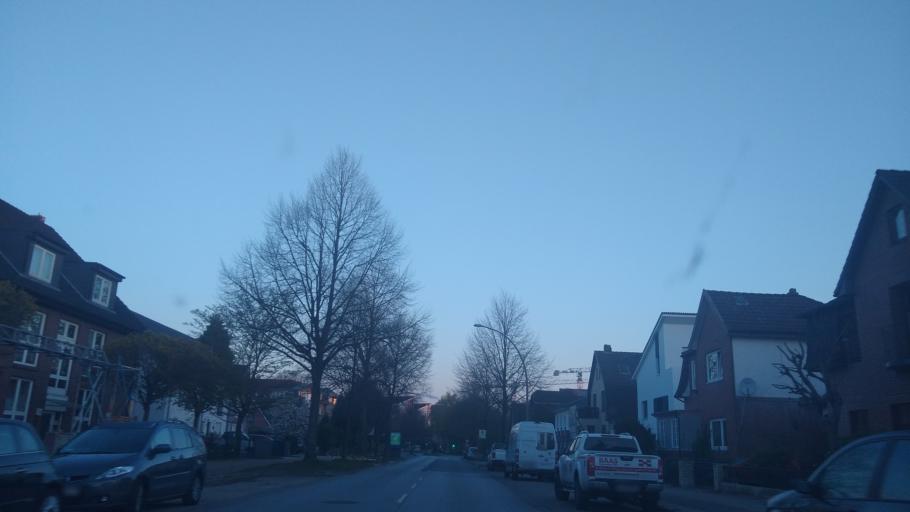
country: DE
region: Schleswig-Holstein
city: Bonningstedt
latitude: 53.6447
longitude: 9.9133
